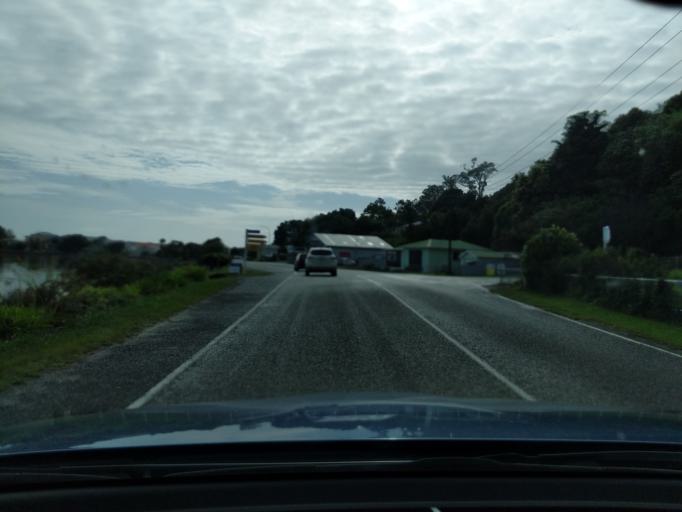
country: NZ
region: Tasman
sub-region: Tasman District
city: Takaka
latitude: -40.6789
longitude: 172.6797
